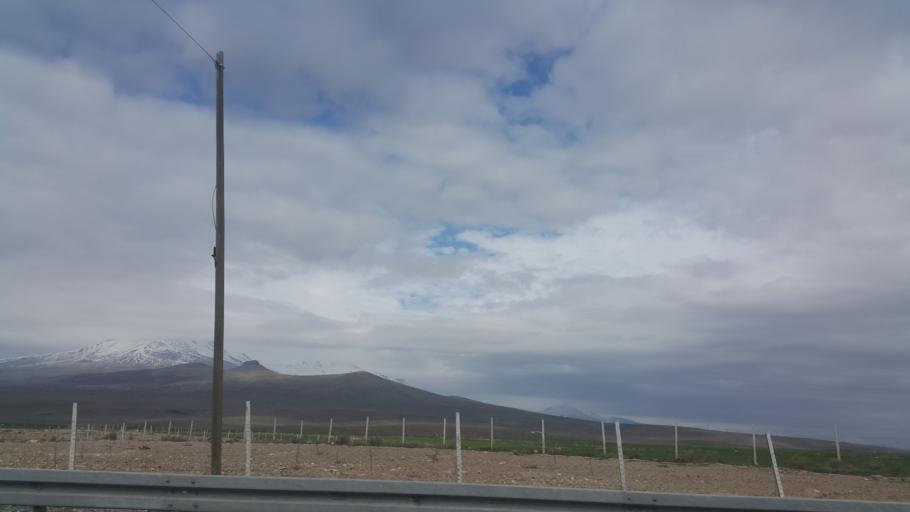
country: TR
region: Aksaray
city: Taspinar
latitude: 38.0272
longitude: 34.0450
